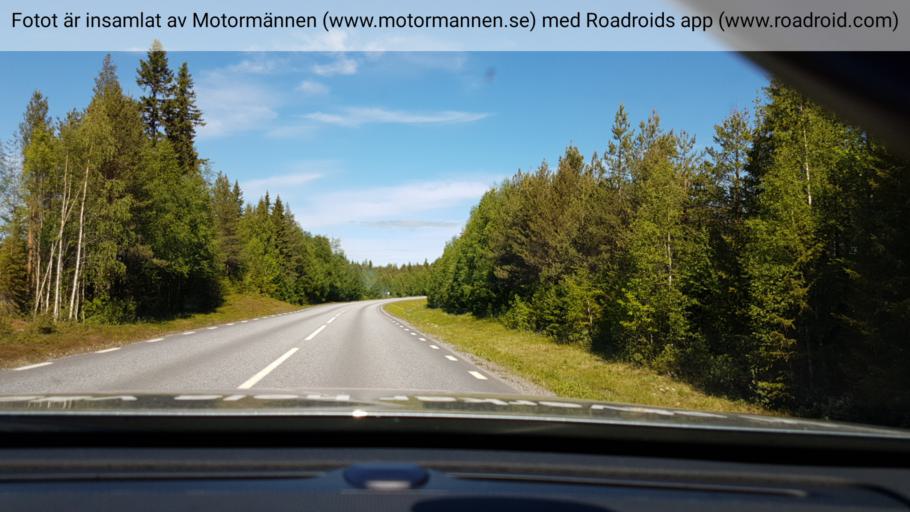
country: SE
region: Vaesterbotten
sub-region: Vilhelmina Kommun
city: Vilhelmina
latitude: 64.5378
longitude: 16.7498
